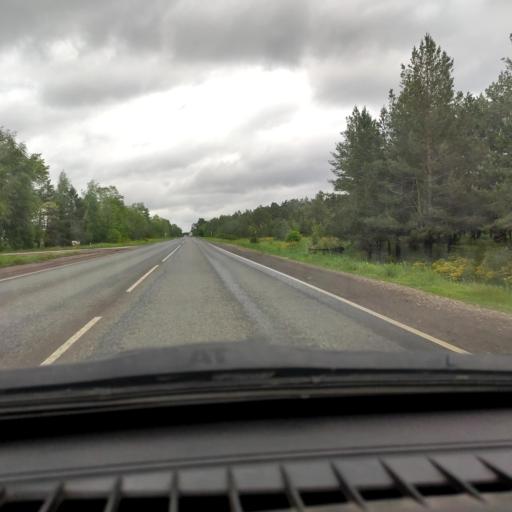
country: RU
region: Samara
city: Povolzhskiy
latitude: 53.6165
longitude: 49.6309
